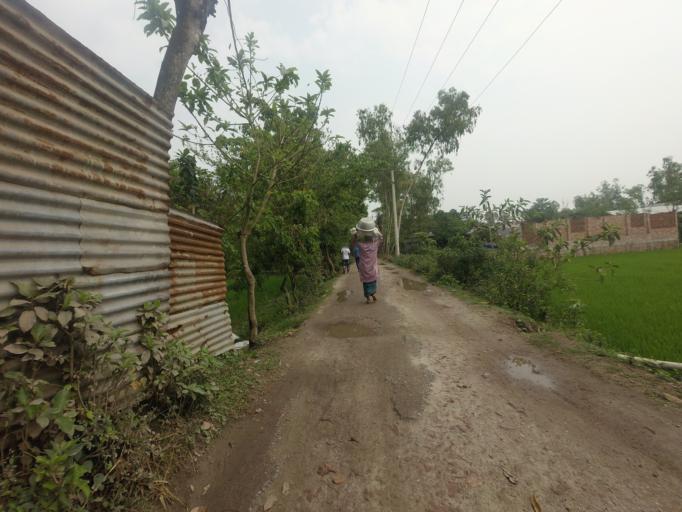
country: BD
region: Rajshahi
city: Sirajganj
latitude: 24.3248
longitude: 89.6867
